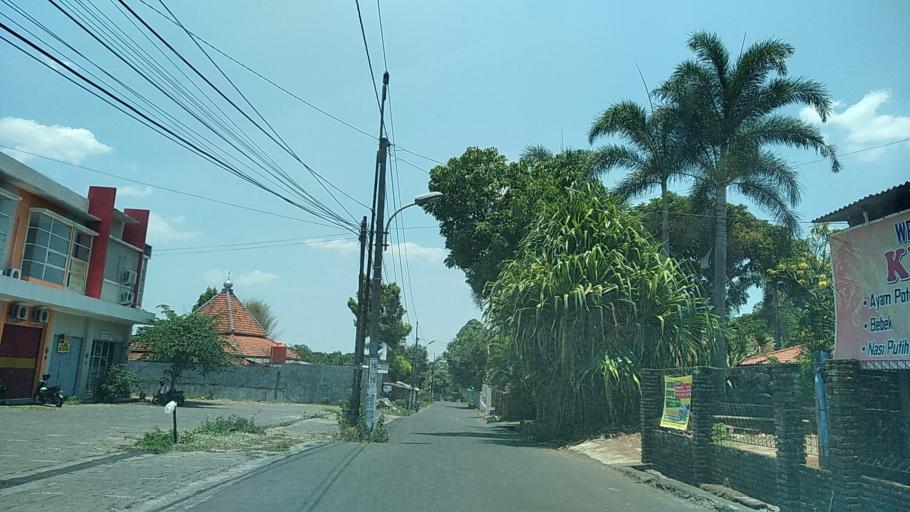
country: ID
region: Central Java
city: Ungaran
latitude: -7.0788
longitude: 110.4213
